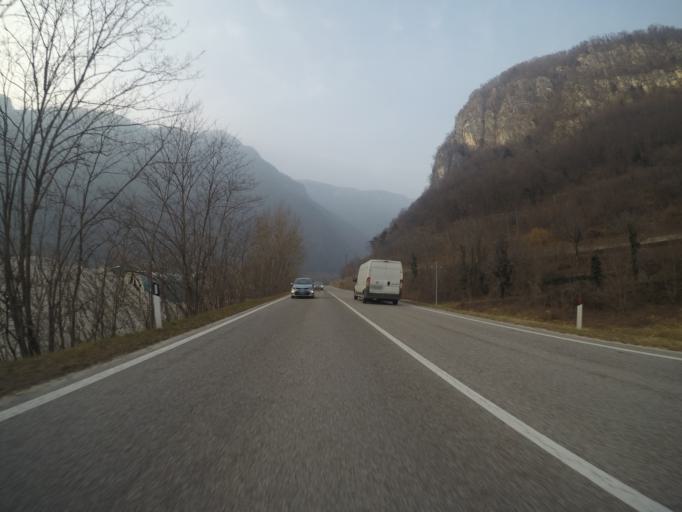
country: IT
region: Veneto
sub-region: Provincia di Belluno
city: Vas
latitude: 45.9394
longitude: 11.9256
